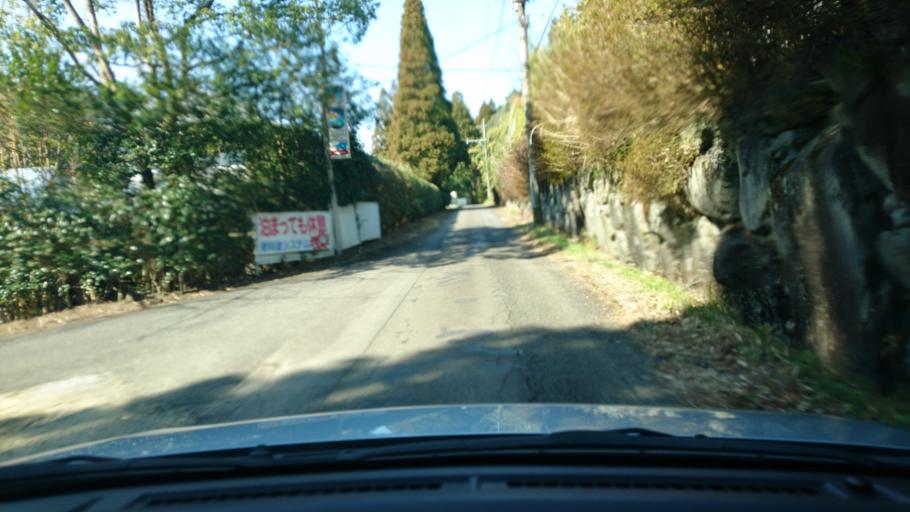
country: JP
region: Miyazaki
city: Miyazaki-shi
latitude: 31.8277
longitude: 131.3928
